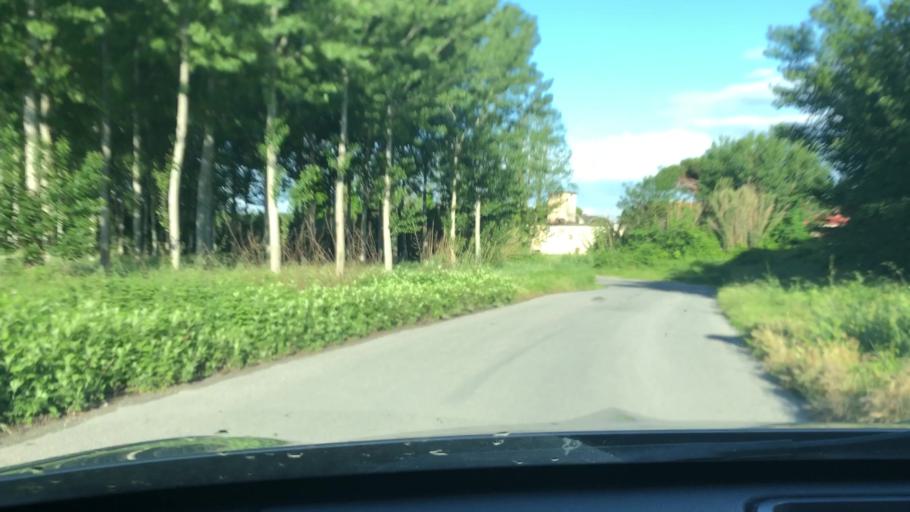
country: IT
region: Tuscany
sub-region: Province of Pisa
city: Forcoli
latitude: 43.6028
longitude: 10.7034
